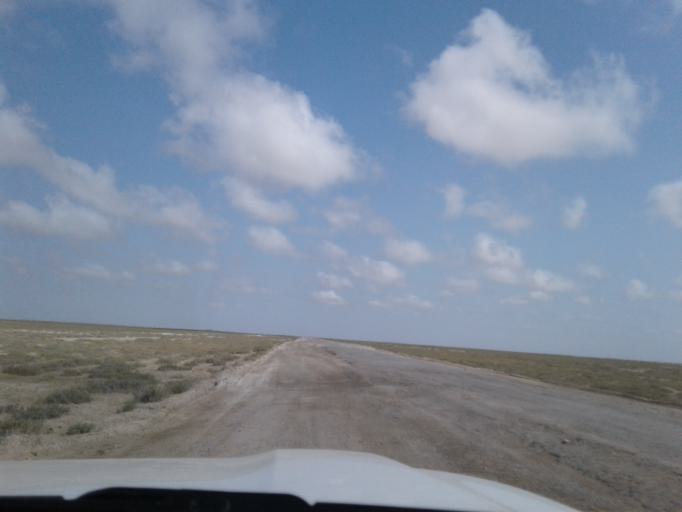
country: IR
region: Golestan
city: Gomishan
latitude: 37.6079
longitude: 53.9253
